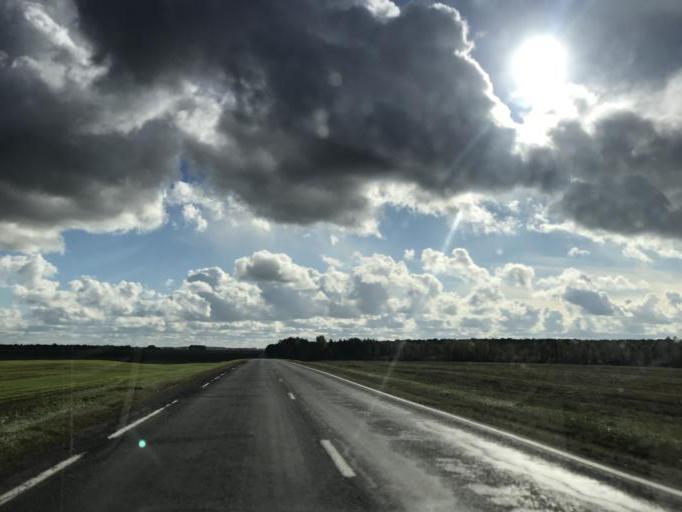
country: BY
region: Gomel
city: Buda-Kashalyova
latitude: 52.8516
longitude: 30.6975
